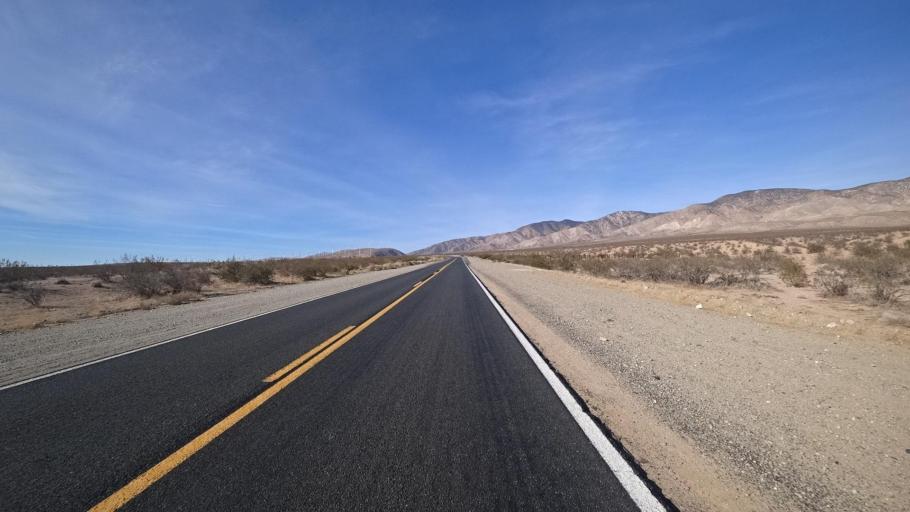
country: US
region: California
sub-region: Kern County
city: Mojave
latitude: 35.1260
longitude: -118.1710
